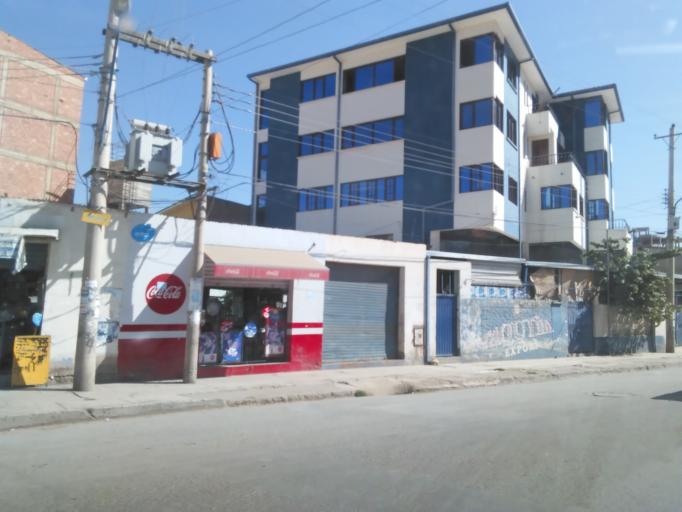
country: BO
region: Cochabamba
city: Cochabamba
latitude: -17.4132
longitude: -66.1513
